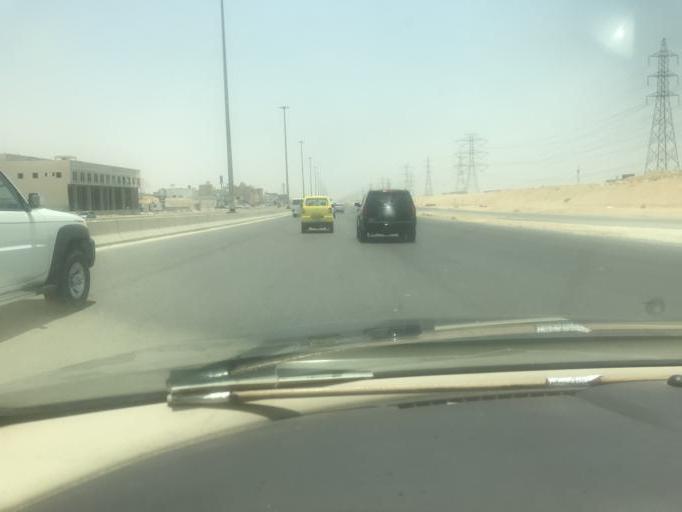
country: SA
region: Ar Riyad
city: Riyadh
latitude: 24.8183
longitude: 46.7354
